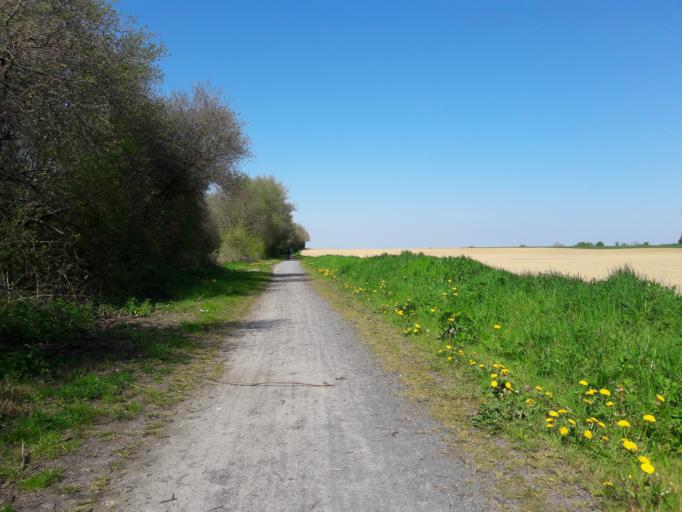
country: FR
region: Nord-Pas-de-Calais
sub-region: Departement du Nord
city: Sains-du-Nord
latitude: 50.1552
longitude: 4.0699
